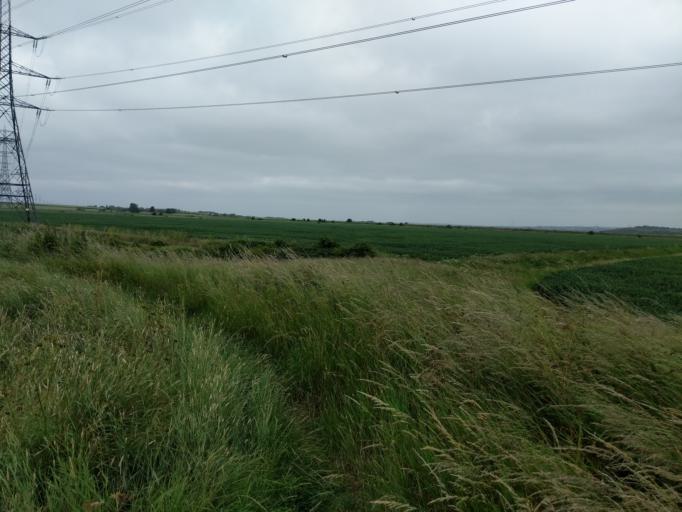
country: GB
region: England
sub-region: Kent
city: Faversham
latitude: 51.3372
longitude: 0.9053
